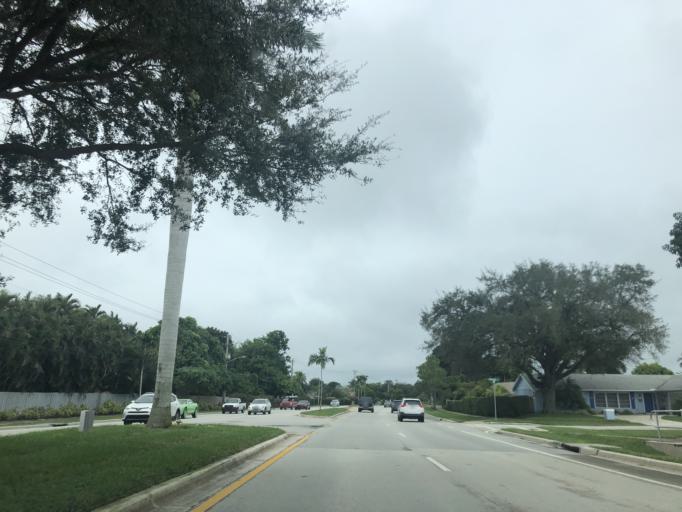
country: US
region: Florida
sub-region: Palm Beach County
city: Wellington
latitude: 26.6646
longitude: -80.2445
